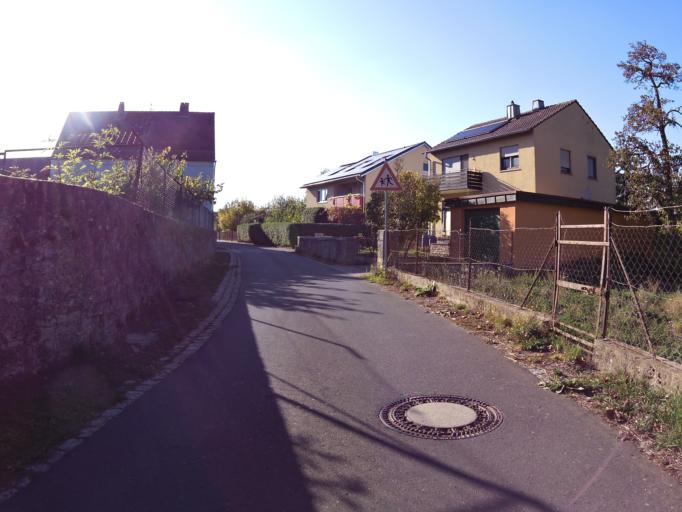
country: DE
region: Bavaria
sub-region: Regierungsbezirk Unterfranken
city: Eibelstadt
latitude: 49.6996
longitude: 9.9709
